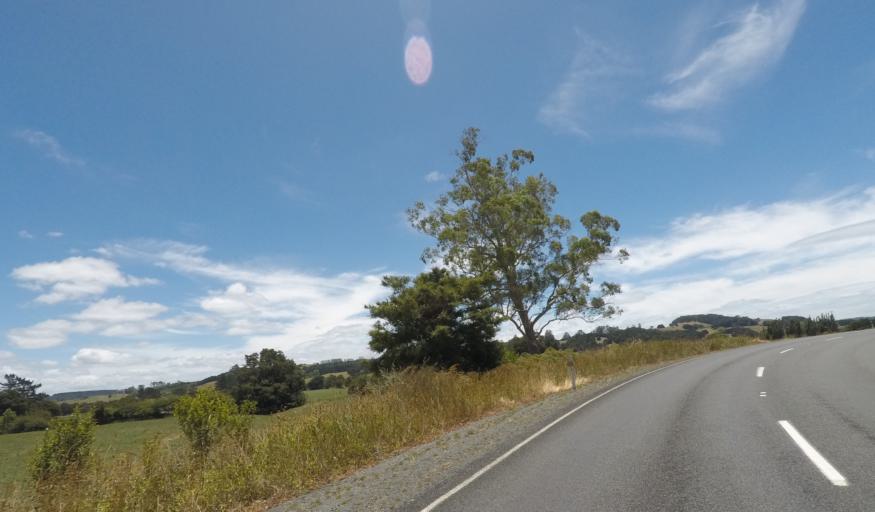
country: NZ
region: Northland
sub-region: Whangarei
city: Whangarei
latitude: -35.5373
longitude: 174.3103
